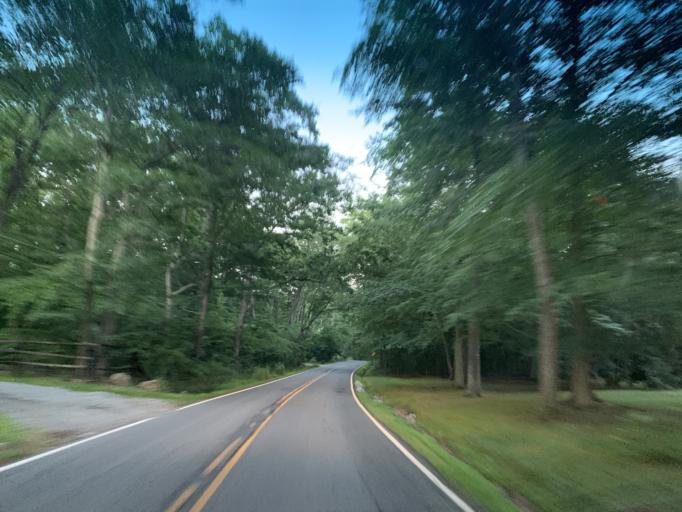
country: US
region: Maryland
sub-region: Cecil County
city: Perryville
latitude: 39.6193
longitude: -76.0519
